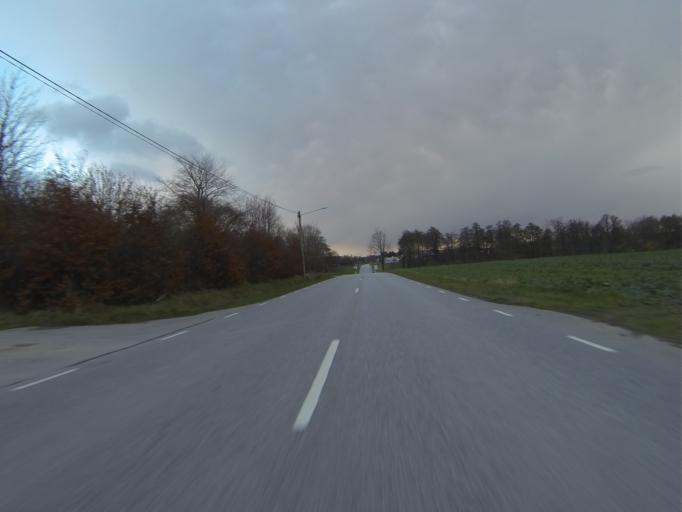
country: SE
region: Skane
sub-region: Lunds Kommun
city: Genarp
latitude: 55.6086
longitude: 13.4048
